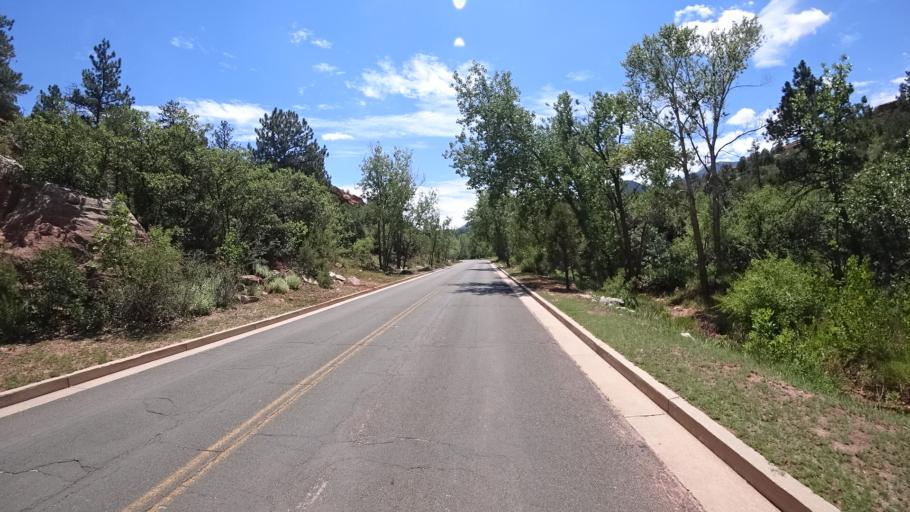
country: US
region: Colorado
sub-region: El Paso County
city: Manitou Springs
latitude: 38.8619
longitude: -104.8995
